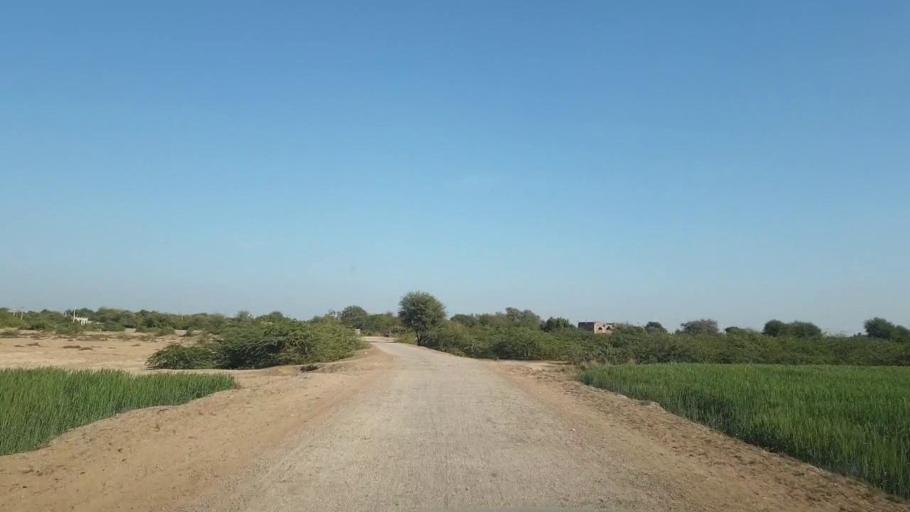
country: PK
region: Sindh
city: Tando Adam
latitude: 25.6869
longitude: 68.6775
